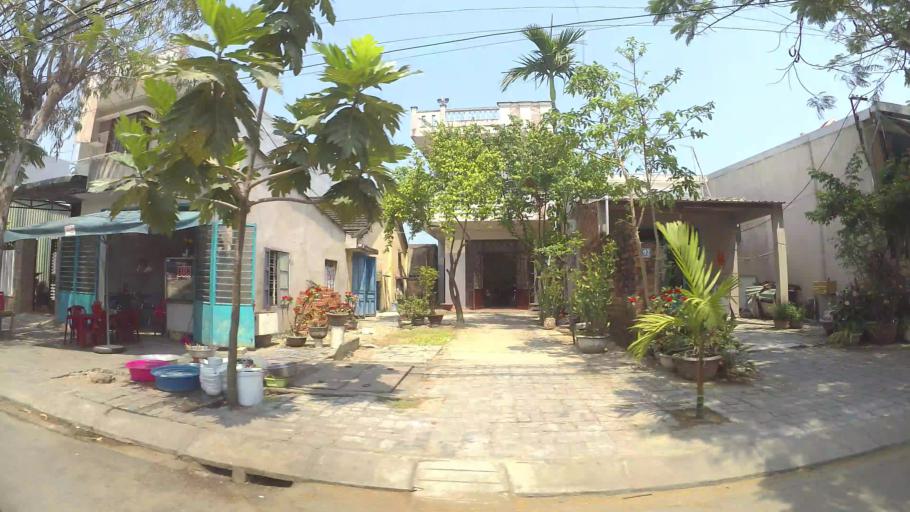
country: VN
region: Da Nang
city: Ngu Hanh Son
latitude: 15.9942
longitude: 108.2650
